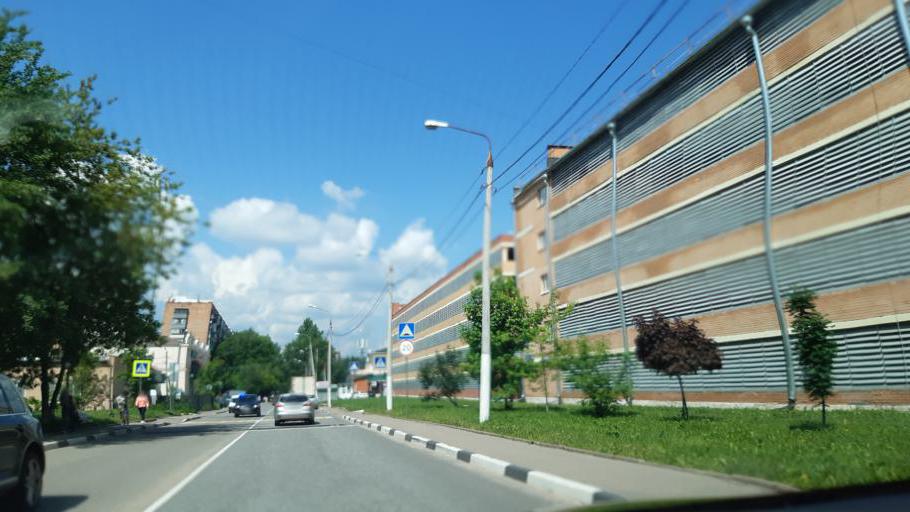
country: RU
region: Moskovskaya
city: Dolgoprudnyy
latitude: 55.9395
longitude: 37.4984
